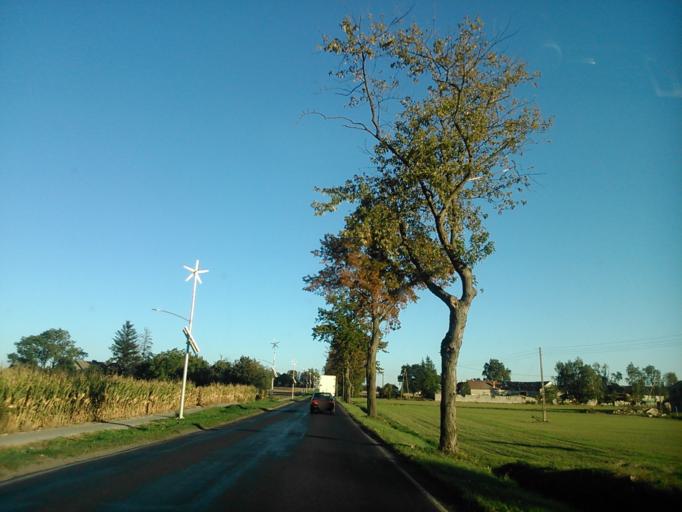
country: PL
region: Kujawsko-Pomorskie
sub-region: Powiat golubsko-dobrzynski
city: Kowalewo Pomorskie
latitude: 53.1559
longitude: 18.9381
